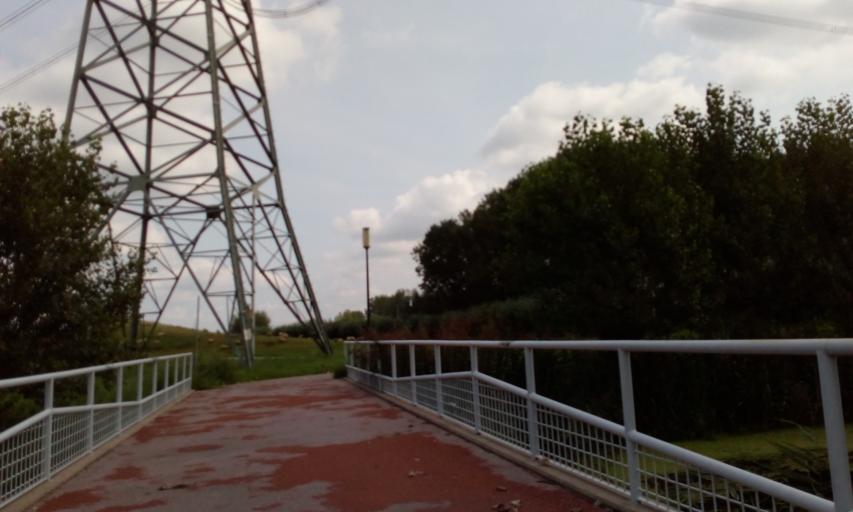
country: NL
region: South Holland
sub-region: Gemeente Capelle aan den IJssel
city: Capelle aan den IJssel
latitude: 51.9656
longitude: 4.5836
